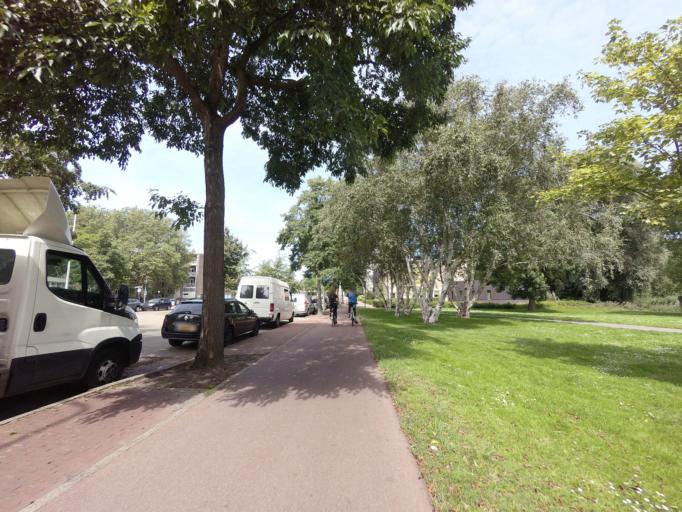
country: NL
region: South Holland
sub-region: Gemeente Den Haag
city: The Hague
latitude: 52.0549
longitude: 4.2770
